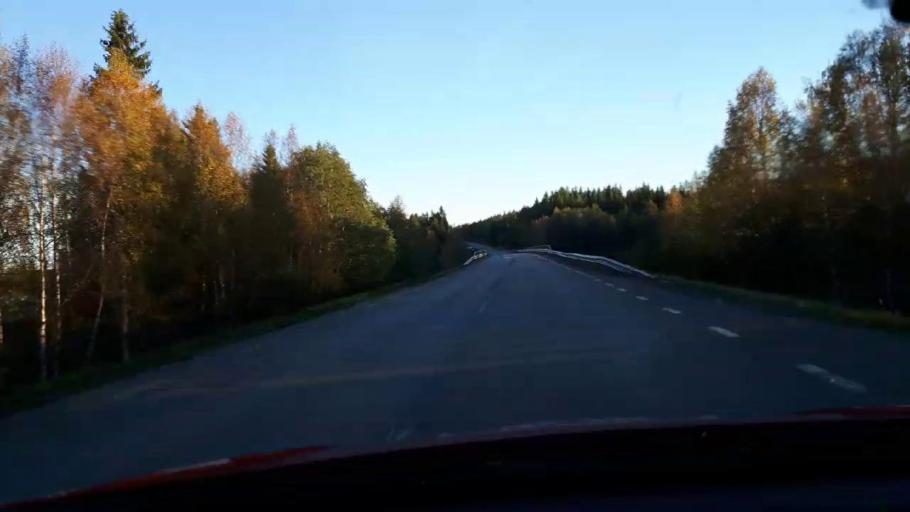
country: SE
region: Jaemtland
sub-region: Krokoms Kommun
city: Krokom
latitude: 63.4554
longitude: 14.4902
